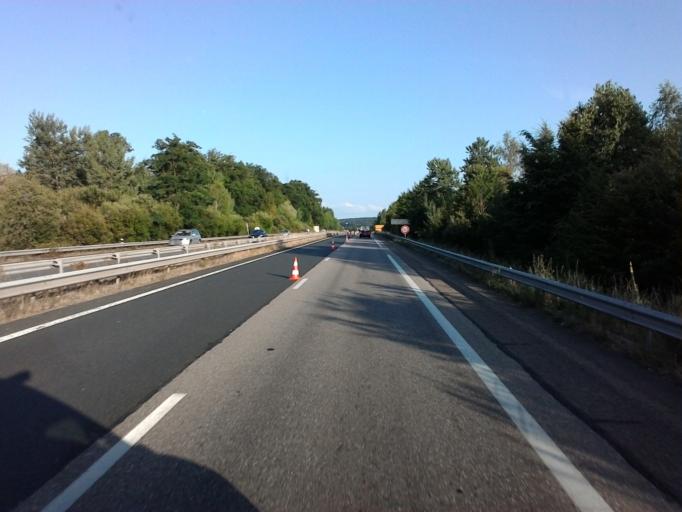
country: FR
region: Lorraine
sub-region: Departement des Vosges
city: Dogneville
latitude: 48.2042
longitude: 6.4648
